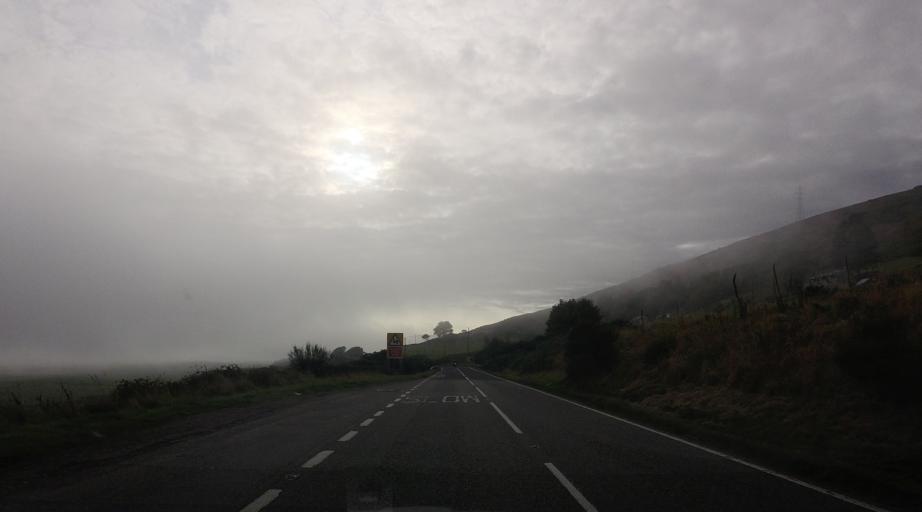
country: GB
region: Scotland
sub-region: Highland
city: Brora
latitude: 58.0799
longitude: -3.7520
